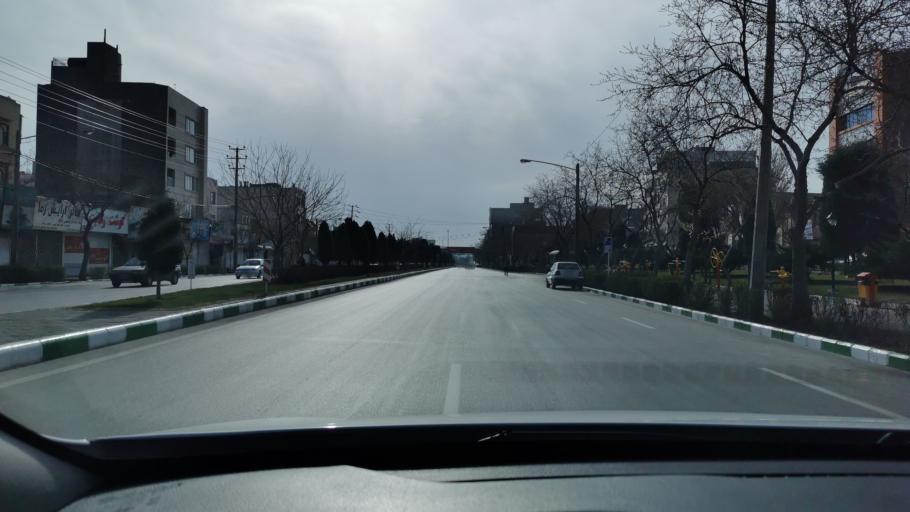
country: IR
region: Razavi Khorasan
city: Mashhad
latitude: 36.2985
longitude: 59.5249
